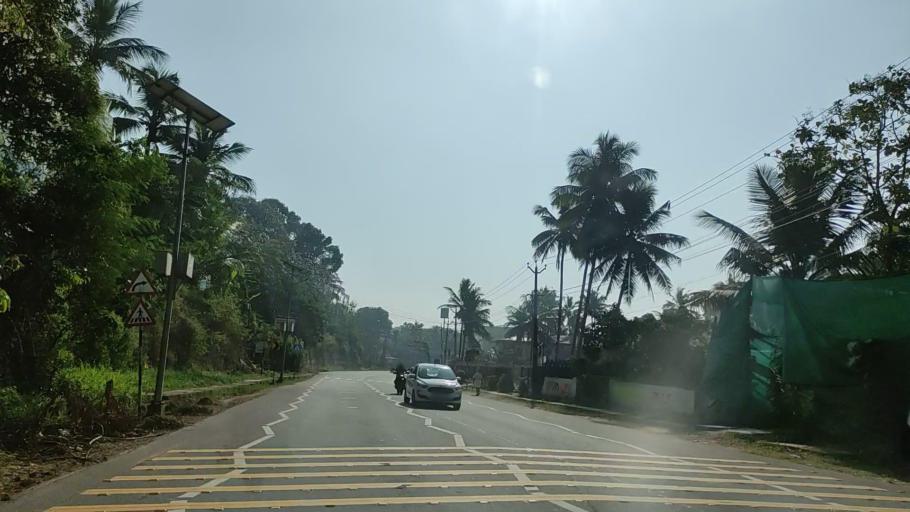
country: IN
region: Kerala
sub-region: Kollam
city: Punalur
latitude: 8.9595
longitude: 76.8405
